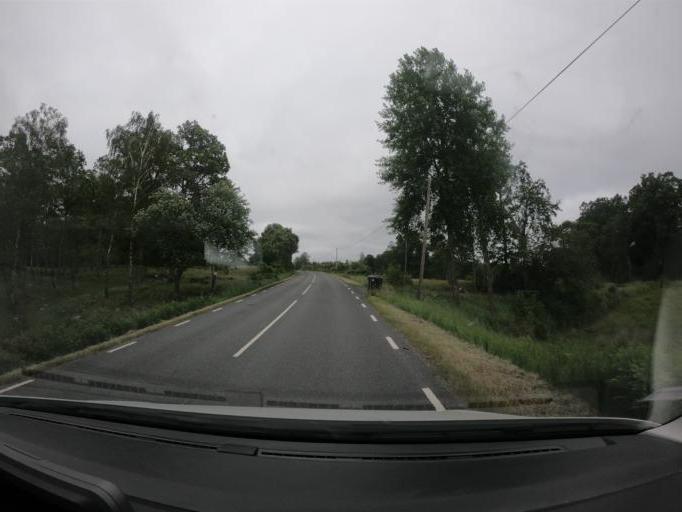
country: SE
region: Skane
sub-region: Perstorps Kommun
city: Perstorp
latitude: 56.1684
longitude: 13.3557
